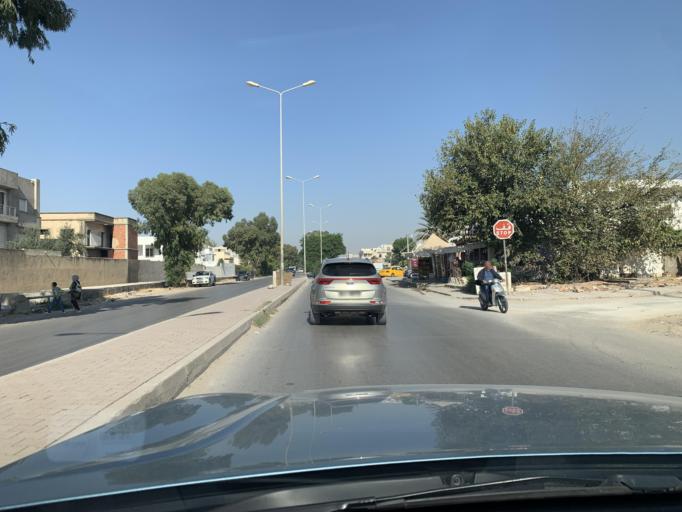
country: TN
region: Manouba
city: Manouba
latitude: 36.8193
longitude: 10.1247
